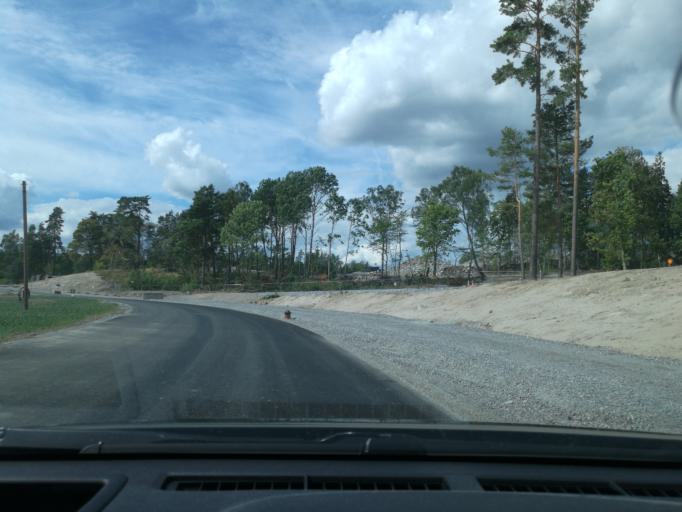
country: SE
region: Stockholm
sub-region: Sigtuna Kommun
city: Marsta
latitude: 59.6065
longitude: 17.8020
